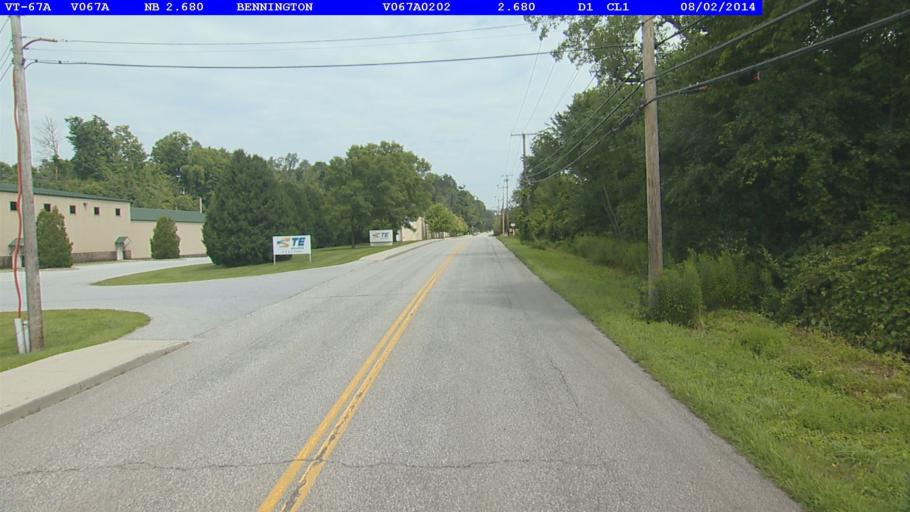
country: US
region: Vermont
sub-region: Bennington County
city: North Bennington
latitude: 42.9212
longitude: -73.2463
